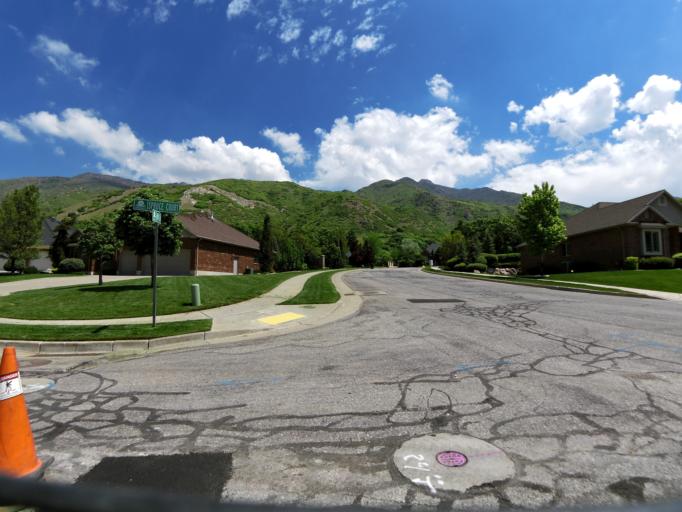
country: US
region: Utah
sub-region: Weber County
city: Uintah
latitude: 41.1636
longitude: -111.9264
